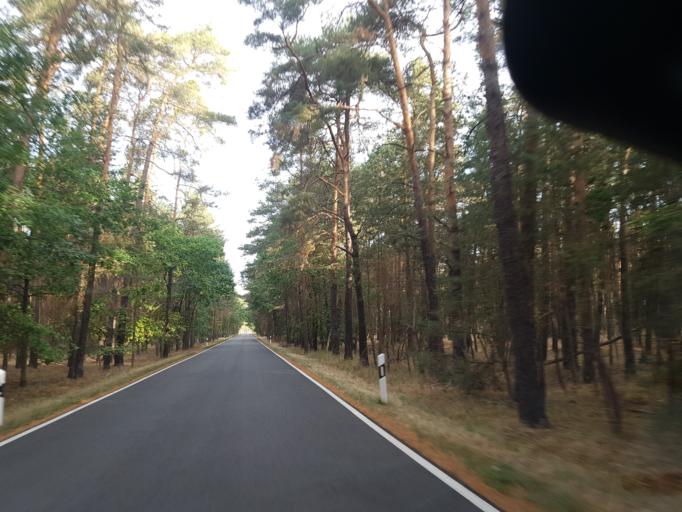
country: DE
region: Saxony-Anhalt
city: Holzdorf
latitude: 51.7981
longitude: 13.0951
